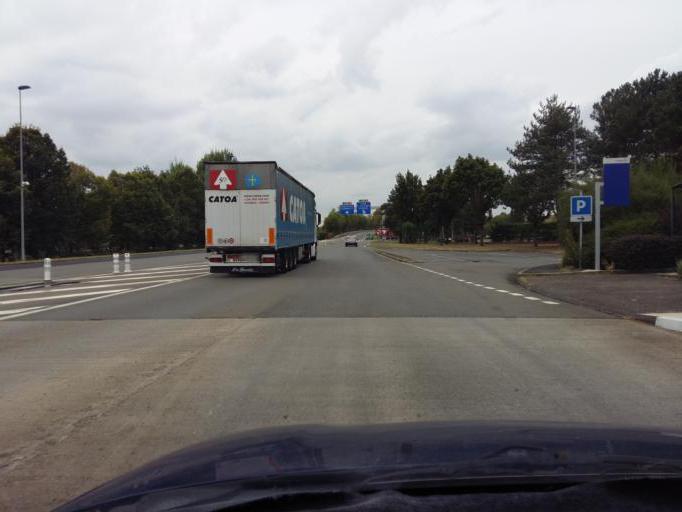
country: FR
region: Auvergne
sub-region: Departement du Puy-de-Dome
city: Peschadoires
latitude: 45.8608
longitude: 3.5013
